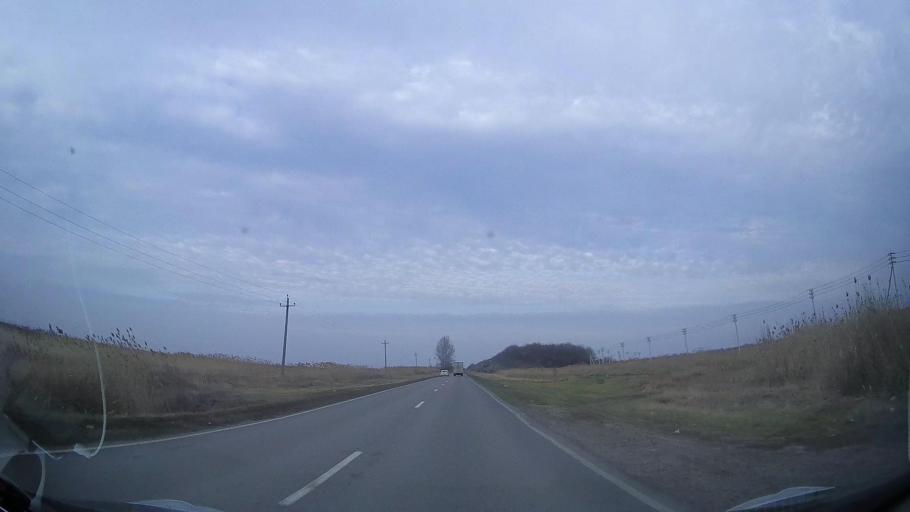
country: RU
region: Rostov
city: Ol'ginskaya
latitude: 47.1429
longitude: 39.9025
